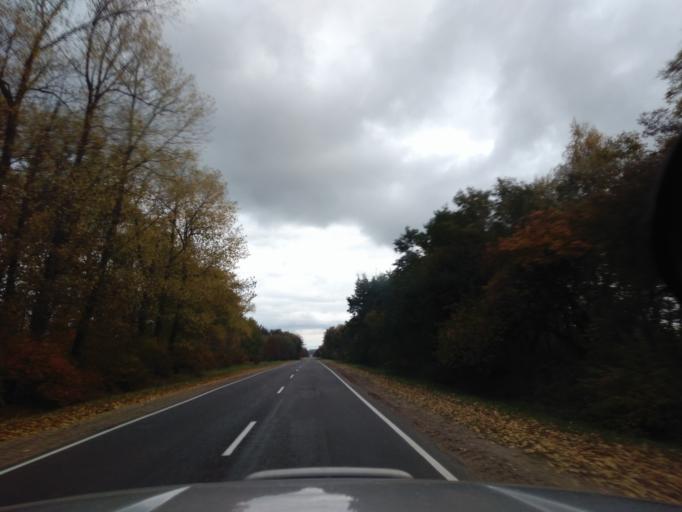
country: BY
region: Minsk
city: Slutsk
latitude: 53.2227
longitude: 27.3671
